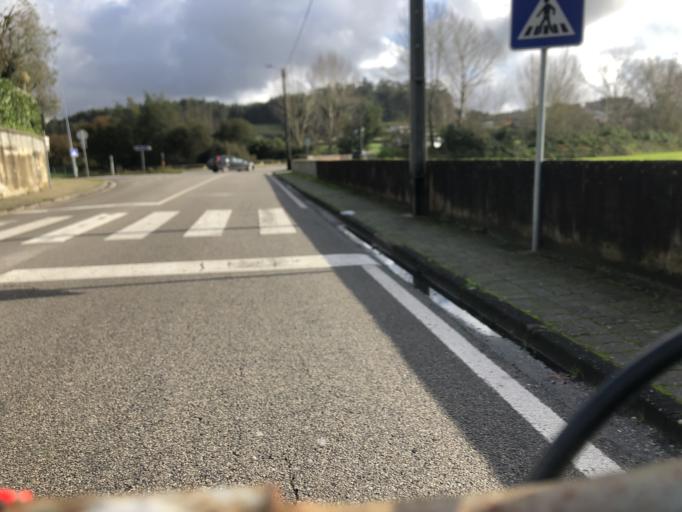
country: PT
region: Aveiro
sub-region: Estarreja
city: Beduido
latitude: 40.7572
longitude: -8.5622
